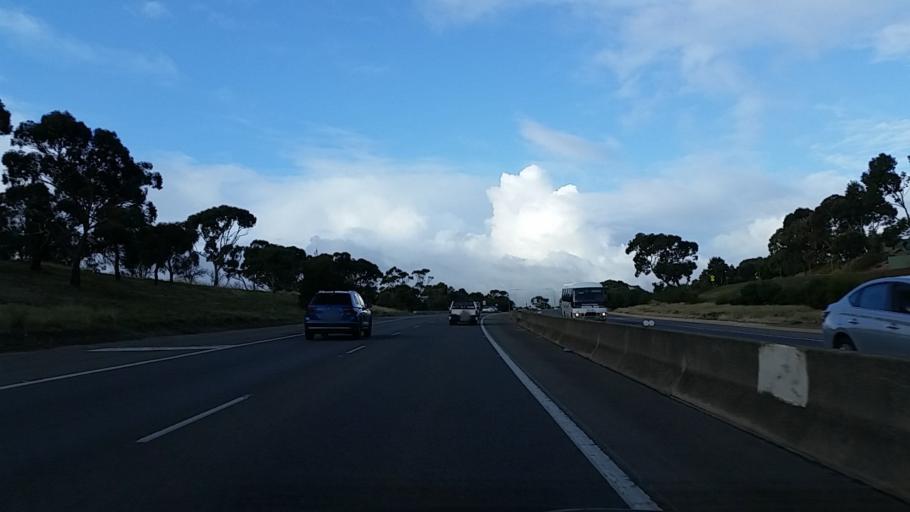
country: AU
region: South Australia
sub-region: Onkaparinga
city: Reynella
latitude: -35.0861
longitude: 138.5025
